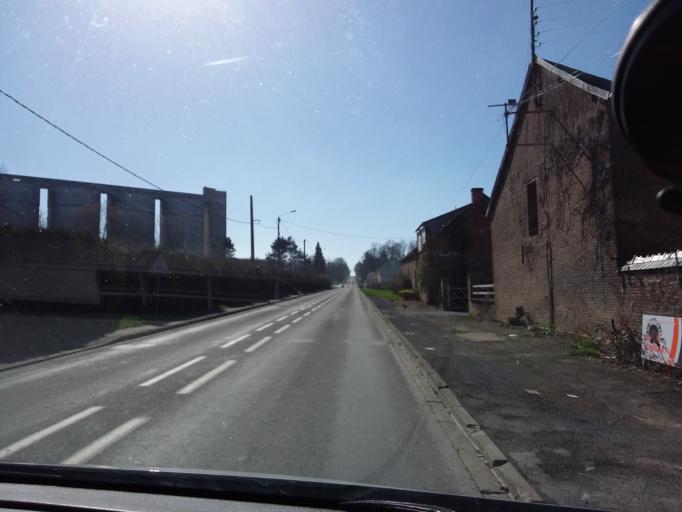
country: FR
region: Picardie
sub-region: Departement de l'Aisne
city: Montcornet
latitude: 49.6933
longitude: 4.0106
